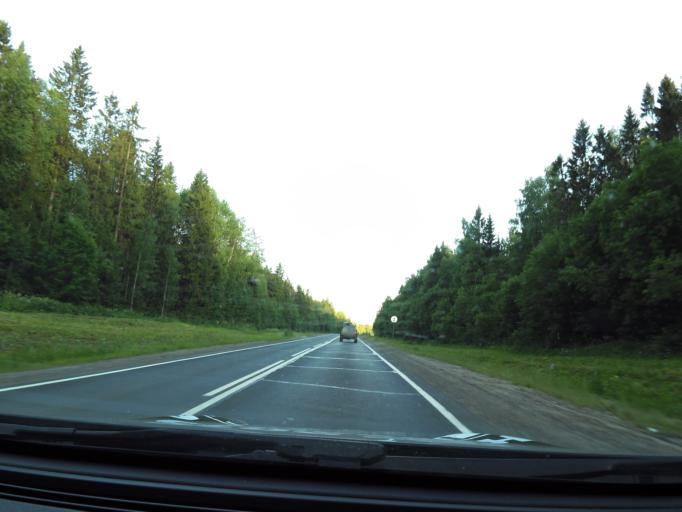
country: RU
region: Vologda
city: Gryazovets
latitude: 58.8742
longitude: 40.1956
